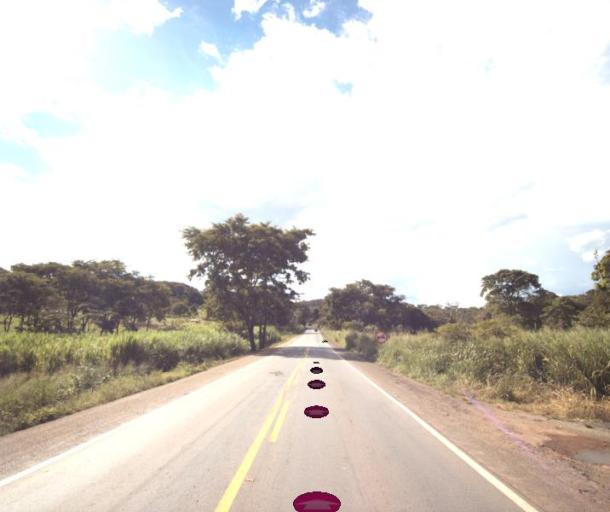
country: BR
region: Goias
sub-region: Jaragua
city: Jaragua
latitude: -15.7072
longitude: -49.3312
